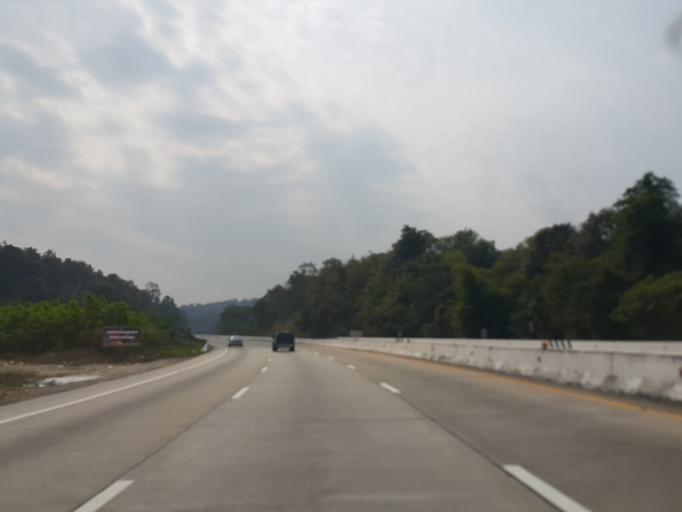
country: TH
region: Lamphun
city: Mae Tha
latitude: 18.4426
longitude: 99.2049
